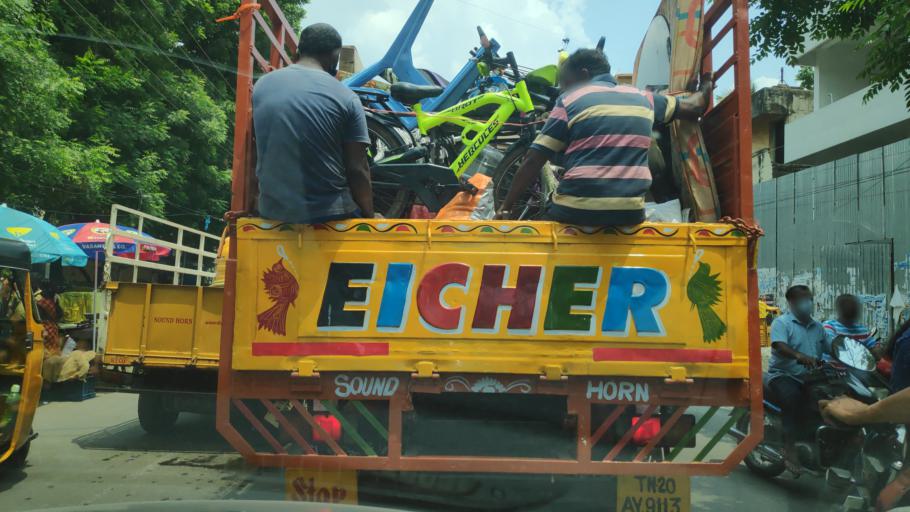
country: IN
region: Tamil Nadu
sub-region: Thiruvallur
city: Ambattur
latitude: 13.1189
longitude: 80.1513
